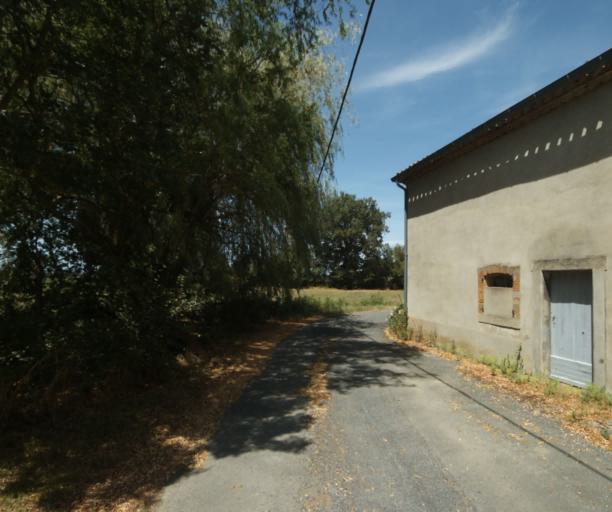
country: FR
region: Midi-Pyrenees
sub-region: Departement du Tarn
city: Soreze
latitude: 43.4924
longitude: 2.0568
